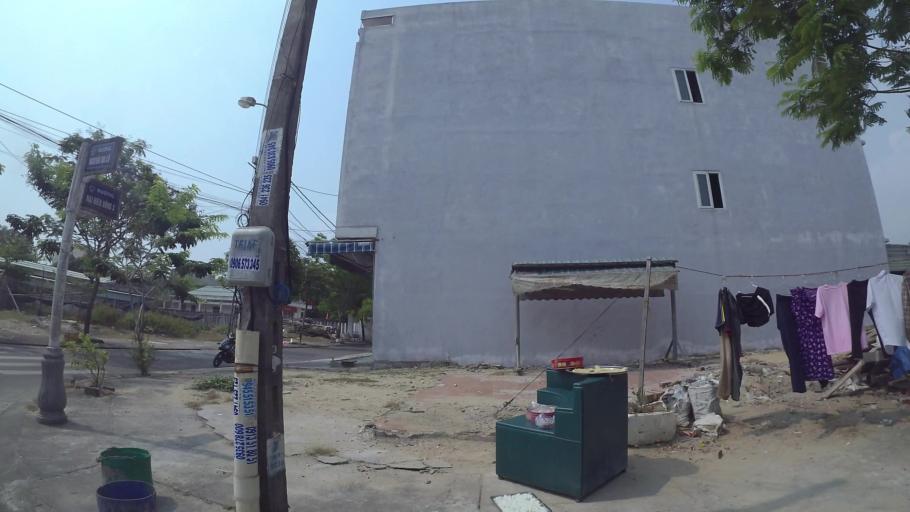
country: VN
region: Da Nang
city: Da Nang
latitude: 16.0924
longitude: 108.2351
